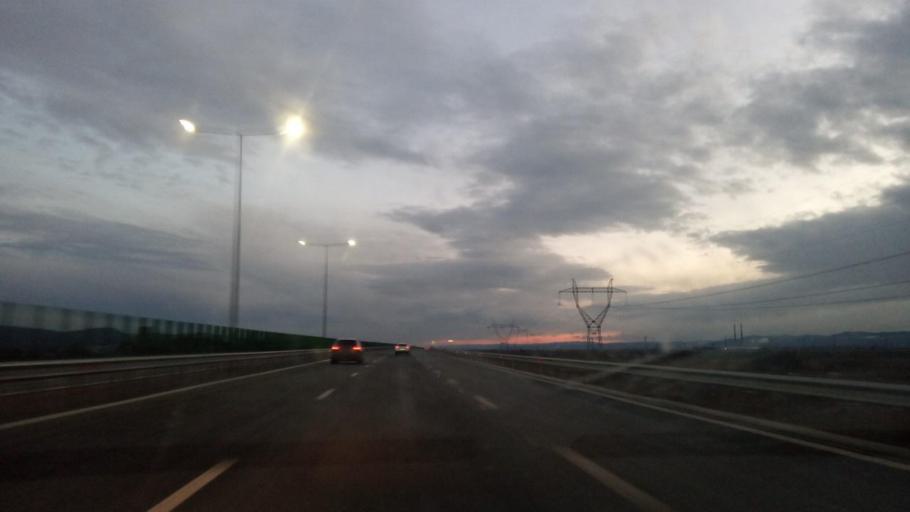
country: RO
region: Bacau
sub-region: Comuna Letea Veche
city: Holt
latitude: 46.5841
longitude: 26.9632
